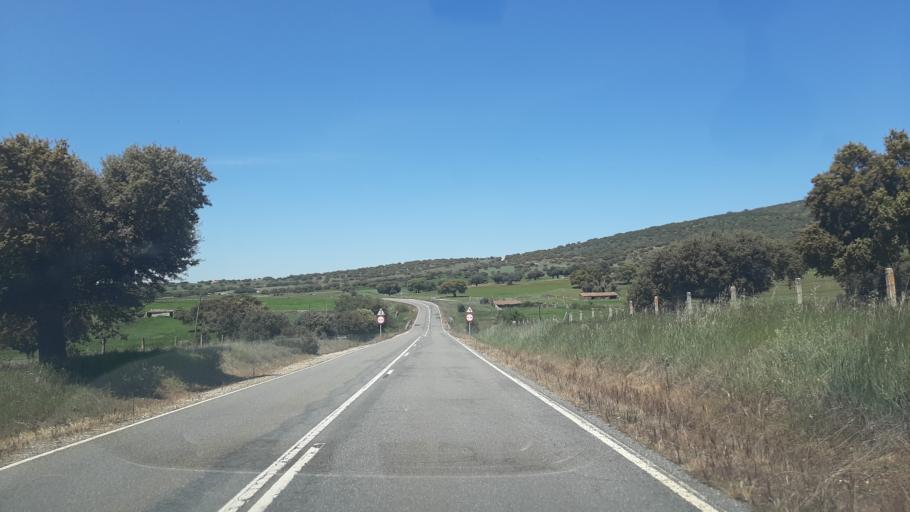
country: ES
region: Castille and Leon
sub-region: Provincia de Salamanca
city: Puente del Congosto
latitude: 40.5345
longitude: -5.5276
